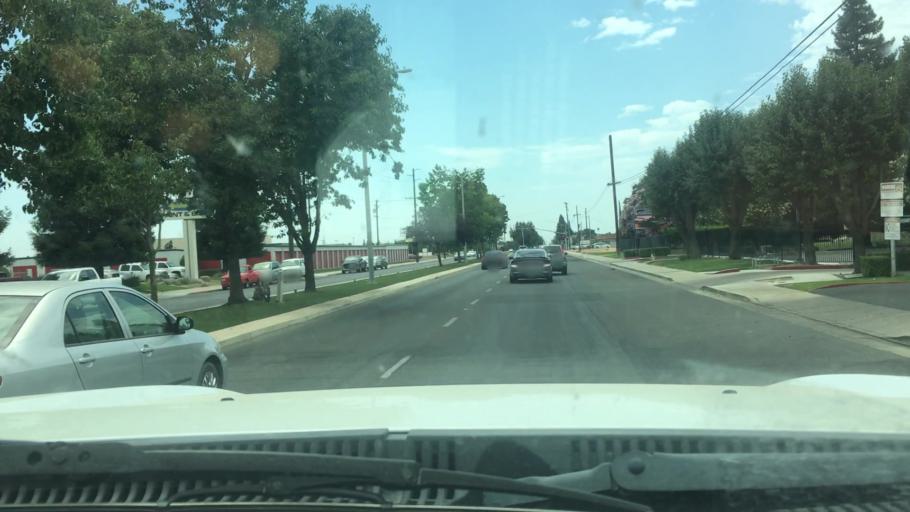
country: US
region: California
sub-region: Tulare County
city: Porterville
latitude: 36.0658
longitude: -119.0591
